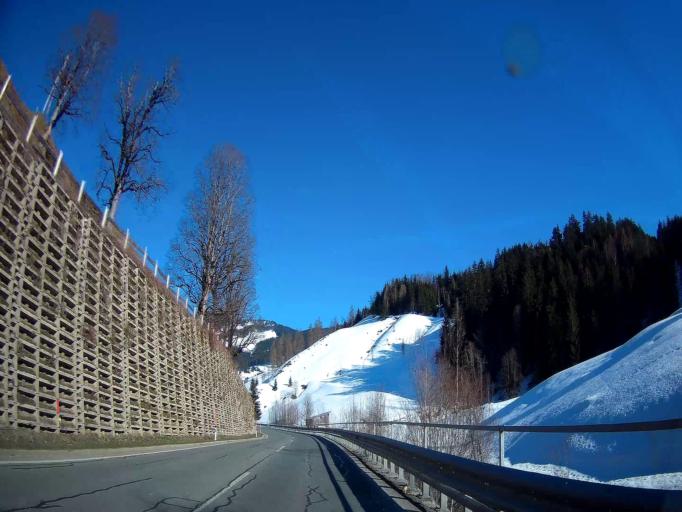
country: AT
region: Salzburg
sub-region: Politischer Bezirk Zell am See
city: Maria Alm am Steinernen Meer
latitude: 47.3858
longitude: 12.9291
